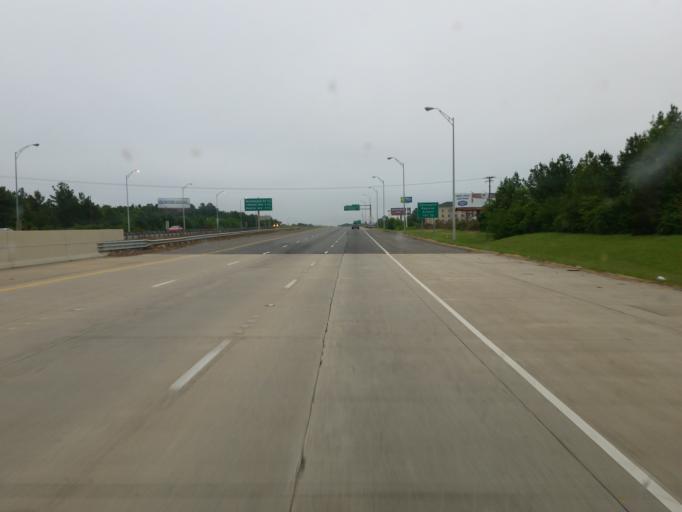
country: US
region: Louisiana
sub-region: Caddo Parish
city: Shreveport
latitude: 32.4587
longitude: -93.8360
